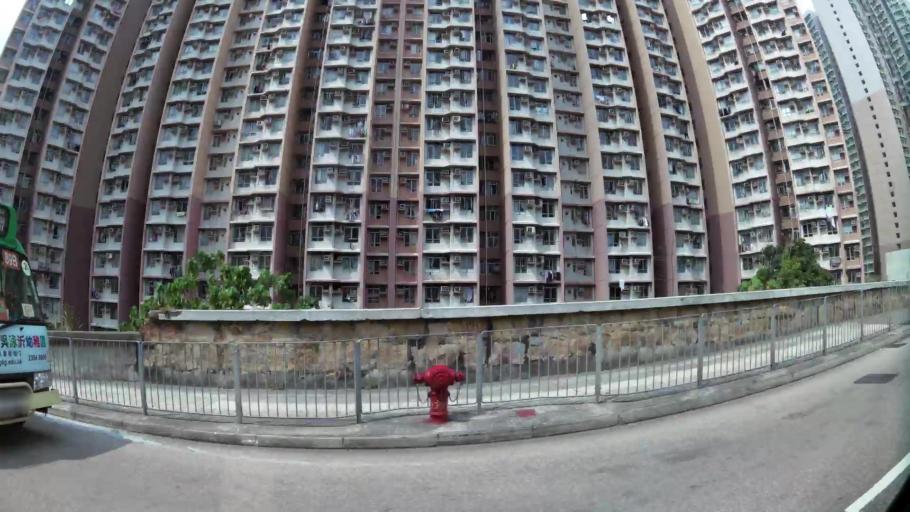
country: HK
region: Kowloon City
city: Kowloon
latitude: 22.3219
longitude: 114.2316
